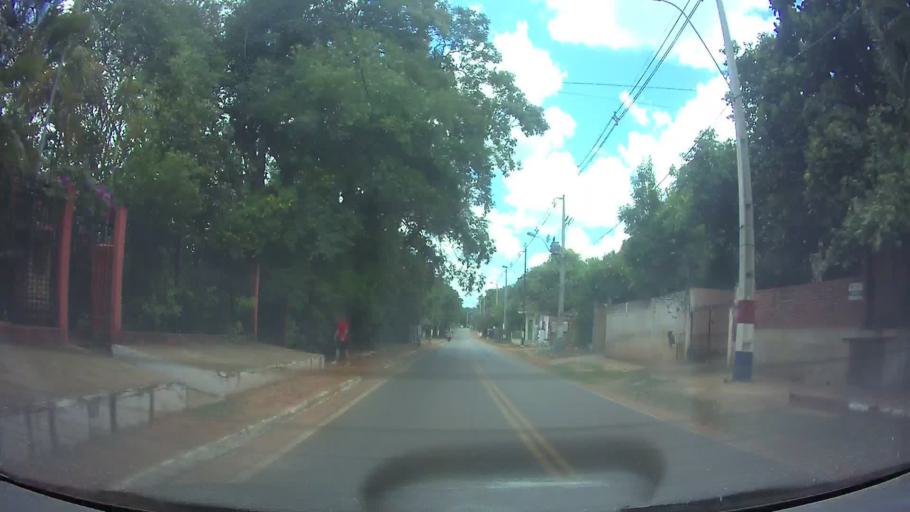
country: PY
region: Central
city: Capiata
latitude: -25.2978
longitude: -57.4416
